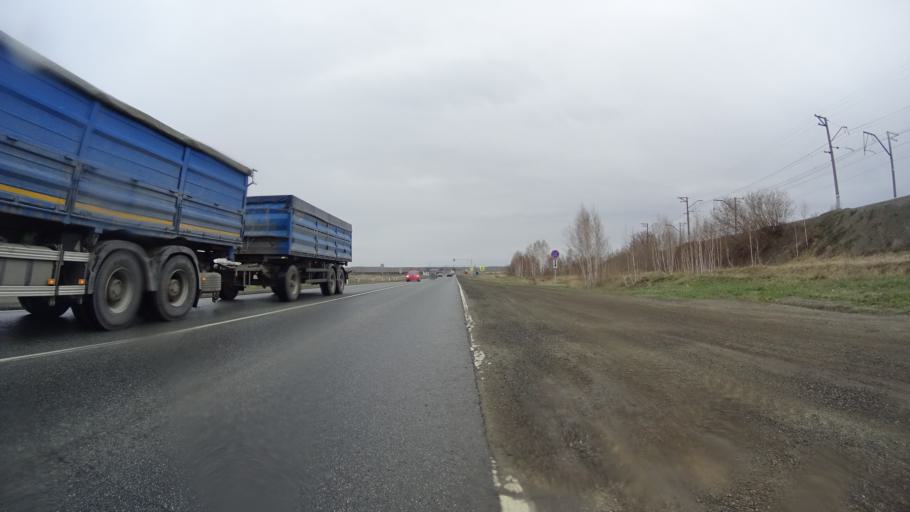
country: RU
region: Chelyabinsk
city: Krasnogorskiy
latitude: 54.6242
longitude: 61.2790
